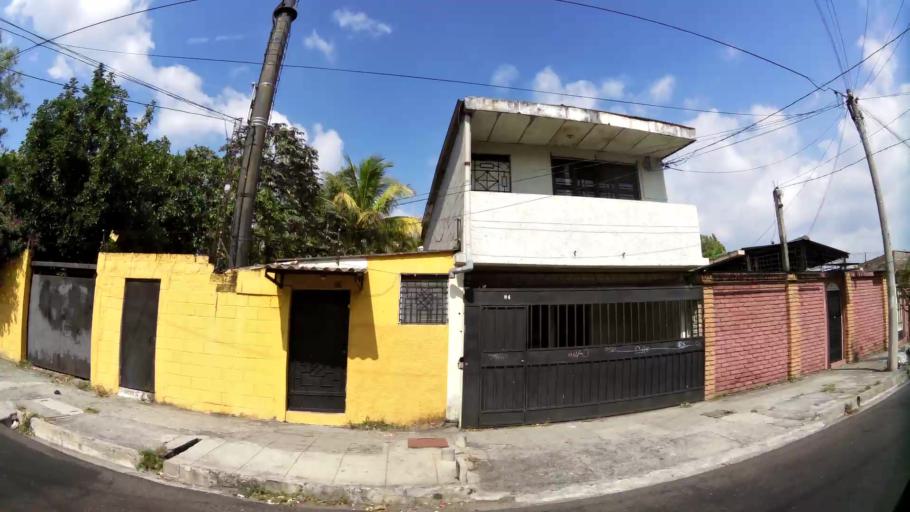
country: SV
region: San Salvador
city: Mejicanos
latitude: 13.7228
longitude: -89.2125
